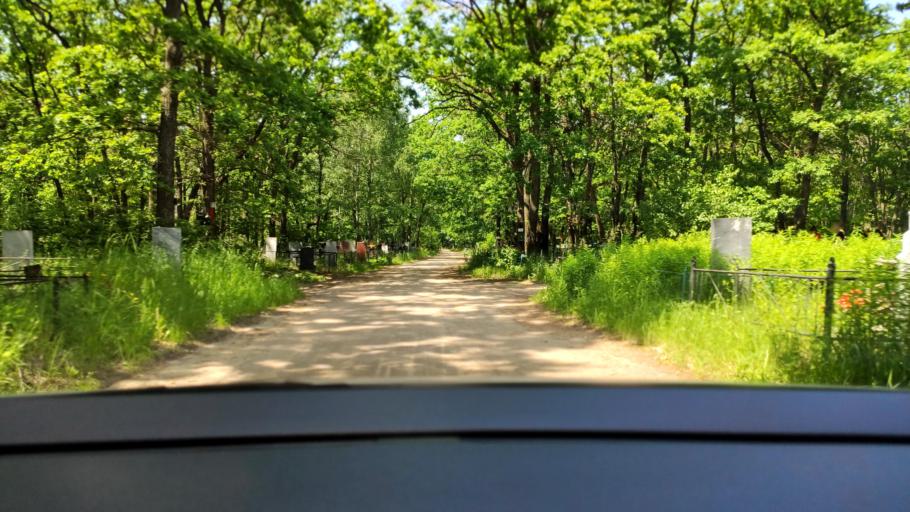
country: RU
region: Voronezj
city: Pridonskoy
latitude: 51.6683
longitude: 39.0898
